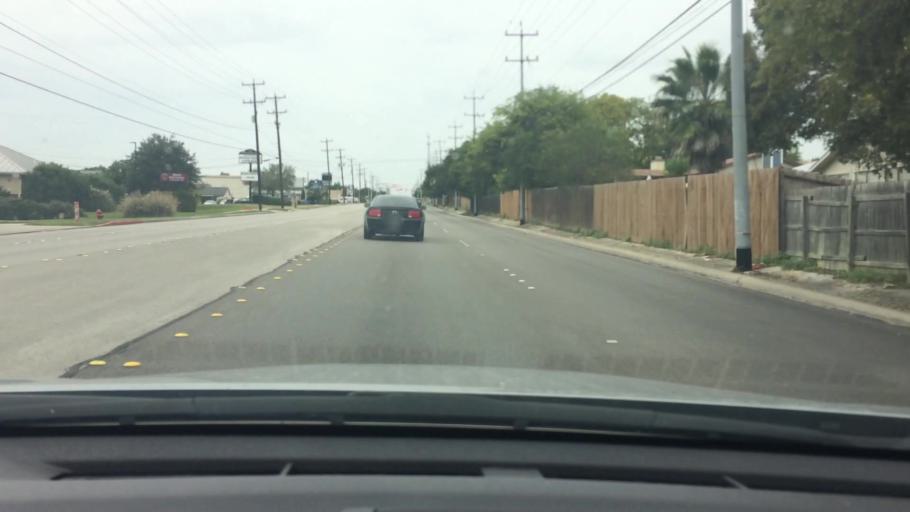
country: US
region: Texas
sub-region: Bexar County
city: Live Oak
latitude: 29.5410
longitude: -98.3387
